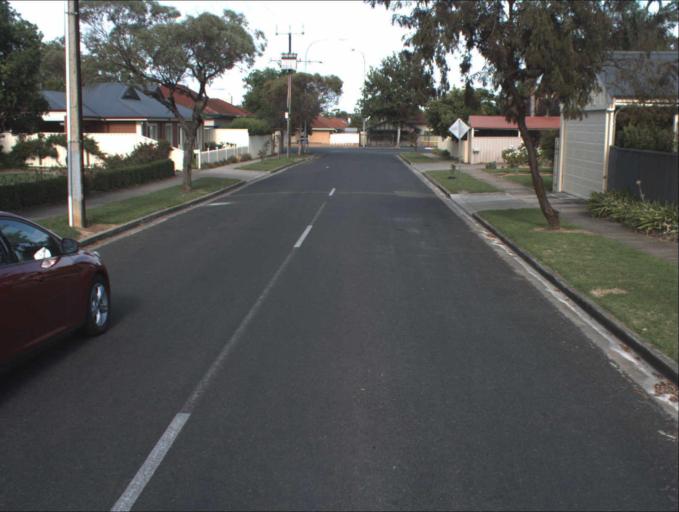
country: AU
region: South Australia
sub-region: Port Adelaide Enfield
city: Klemzig
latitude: -34.8747
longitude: 138.6204
